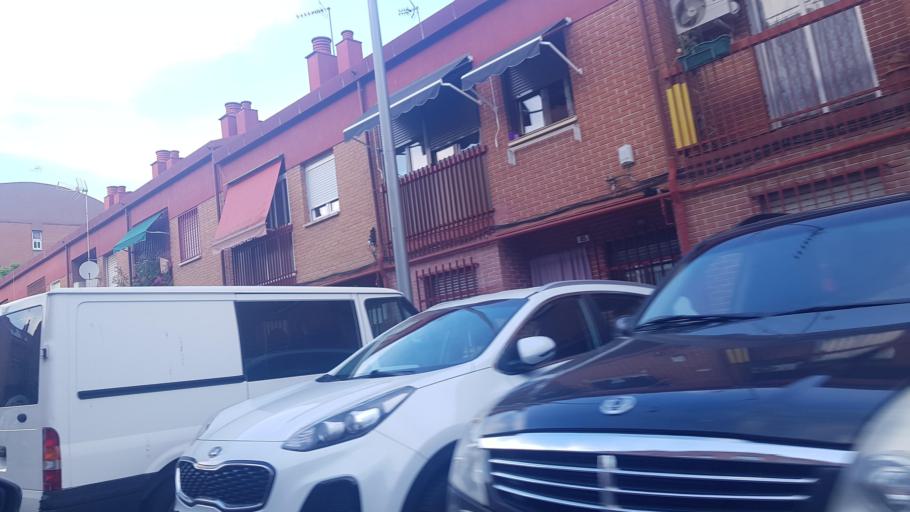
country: ES
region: Madrid
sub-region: Provincia de Madrid
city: Puente de Vallecas
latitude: 40.3716
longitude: -3.6580
